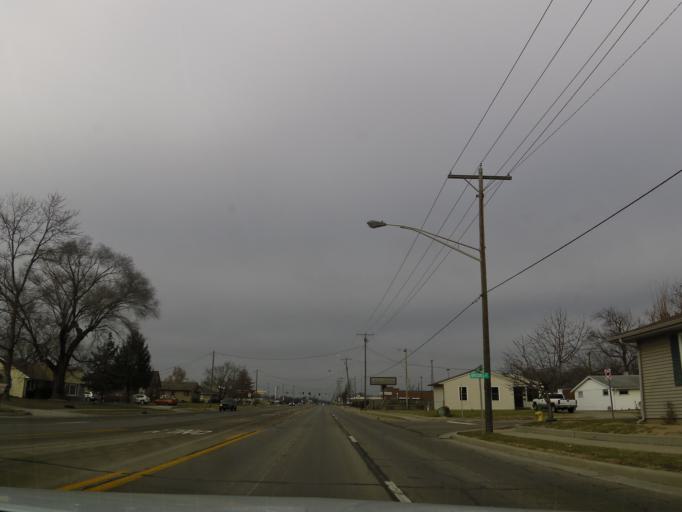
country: US
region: Indiana
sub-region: Bartholomew County
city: Columbus
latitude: 39.1922
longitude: -85.8916
